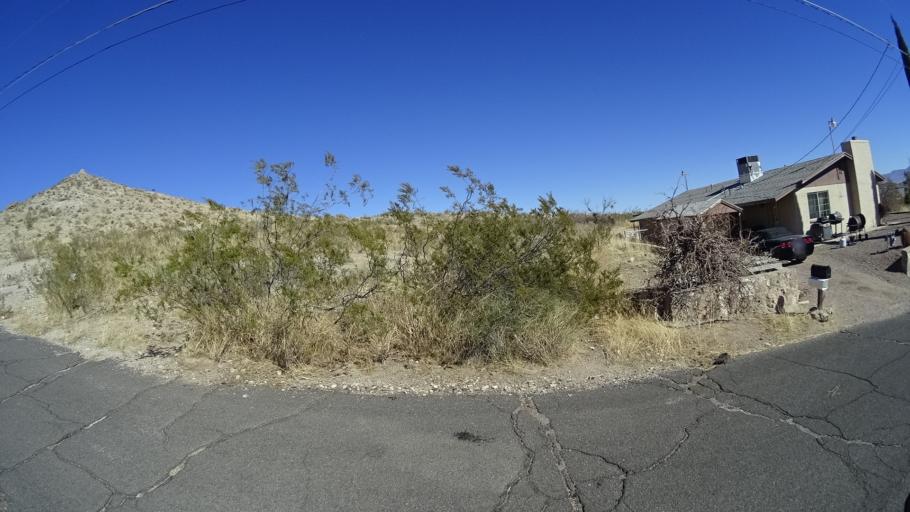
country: US
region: Arizona
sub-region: Mohave County
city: Kingman
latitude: 35.1945
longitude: -114.0365
